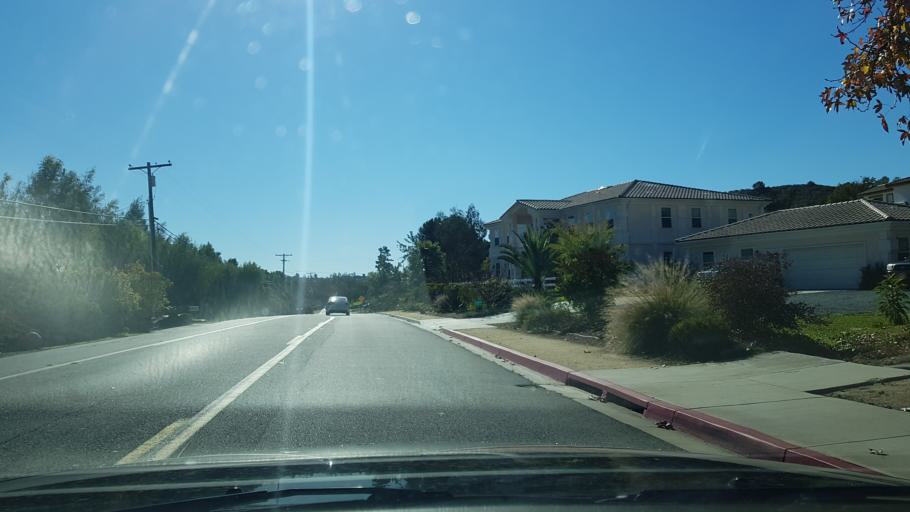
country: US
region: California
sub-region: San Diego County
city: Rancho Santa Fe
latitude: 33.0345
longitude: -117.2397
